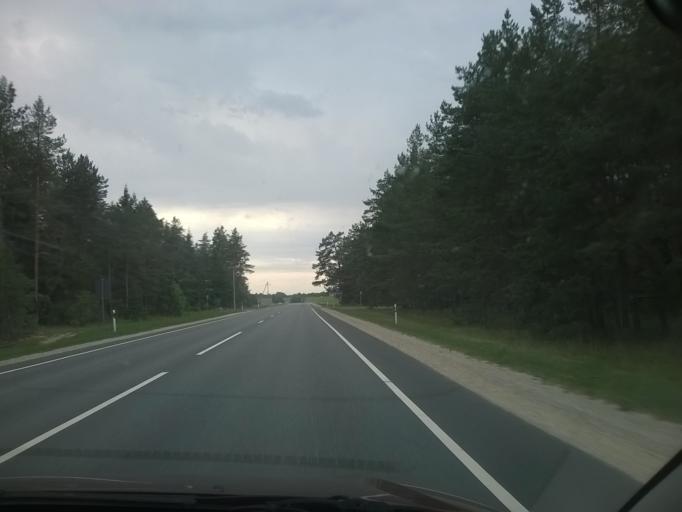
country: EE
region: Harju
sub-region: Nissi vald
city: Turba
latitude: 59.0561
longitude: 24.1862
